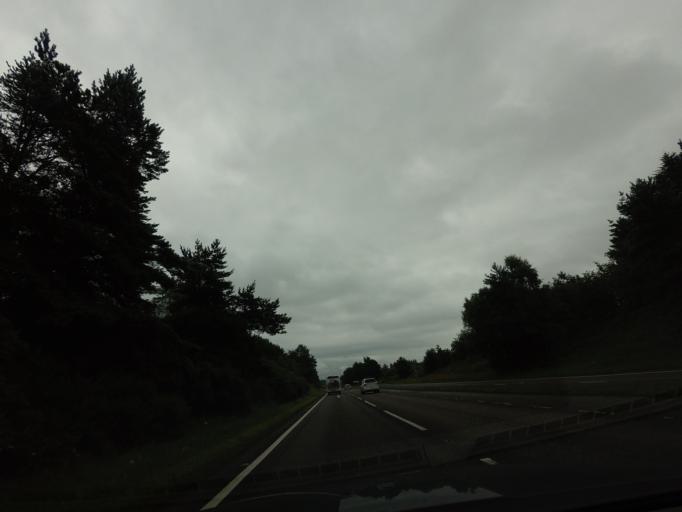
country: GB
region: Scotland
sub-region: Highland
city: Conon Bridge
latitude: 57.5312
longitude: -4.3270
